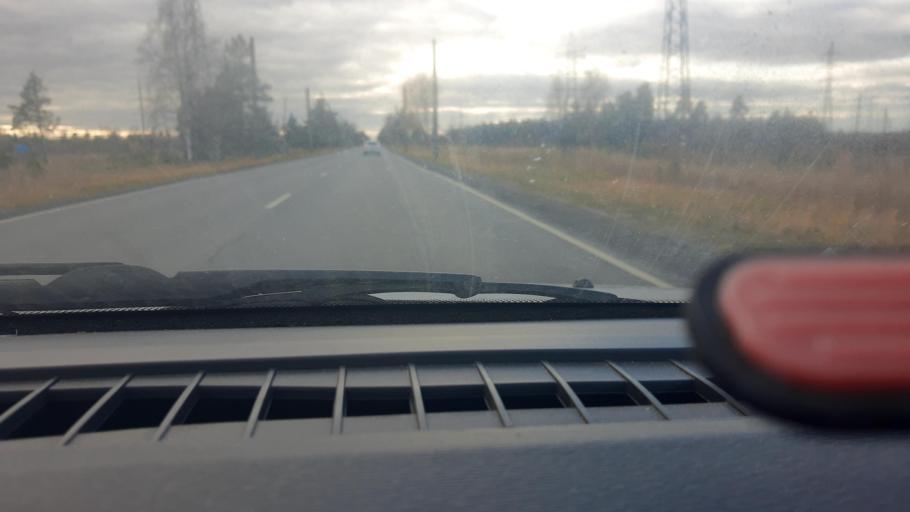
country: RU
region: Nizjnij Novgorod
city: Babino
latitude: 56.2847
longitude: 43.5807
